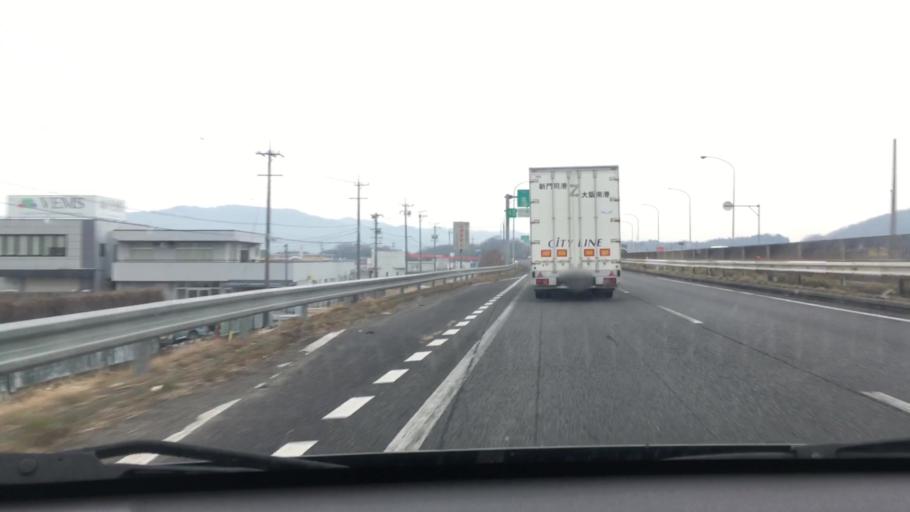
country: JP
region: Mie
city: Ueno-ebisumachi
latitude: 34.7681
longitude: 136.1565
